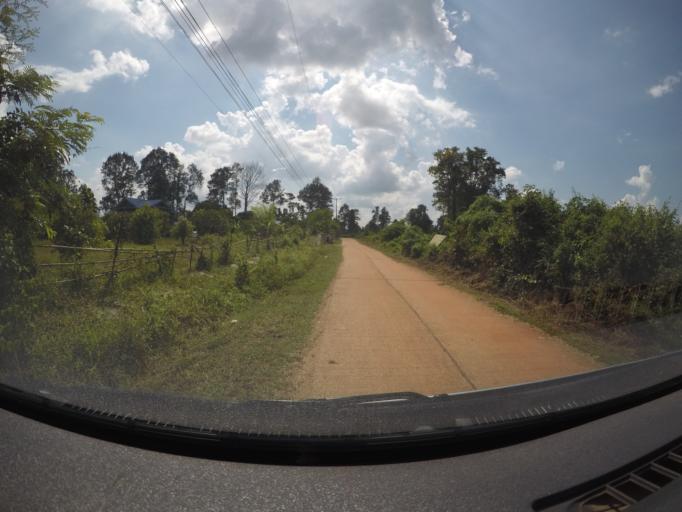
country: TH
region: Sakon Nakhon
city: Sakon Nakhon
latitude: 17.2161
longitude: 104.0861
